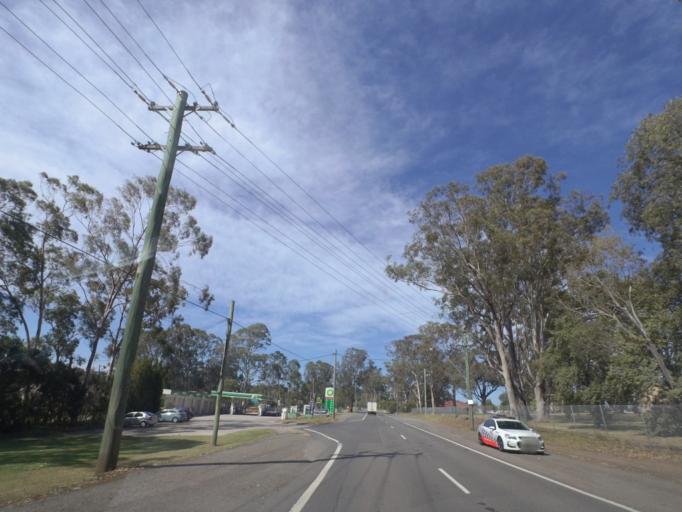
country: AU
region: New South Wales
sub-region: Campbelltown Municipality
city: Denham Court
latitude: -33.9830
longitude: 150.8461
